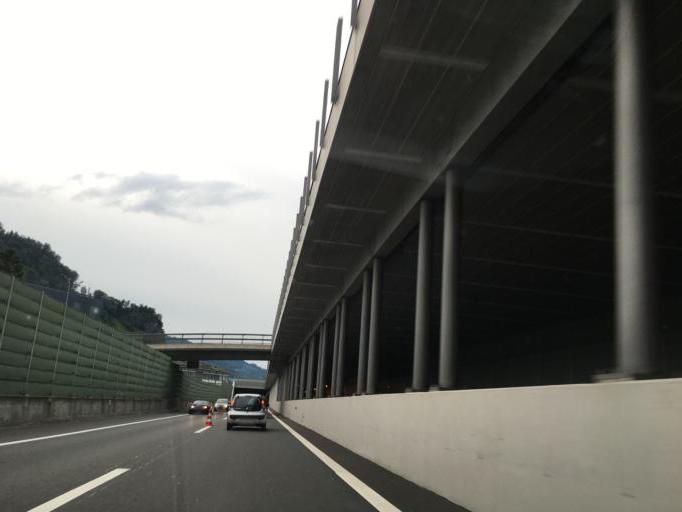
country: CH
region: Nidwalden
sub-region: Nidwalden
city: Stansstad
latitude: 46.9726
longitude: 8.3405
